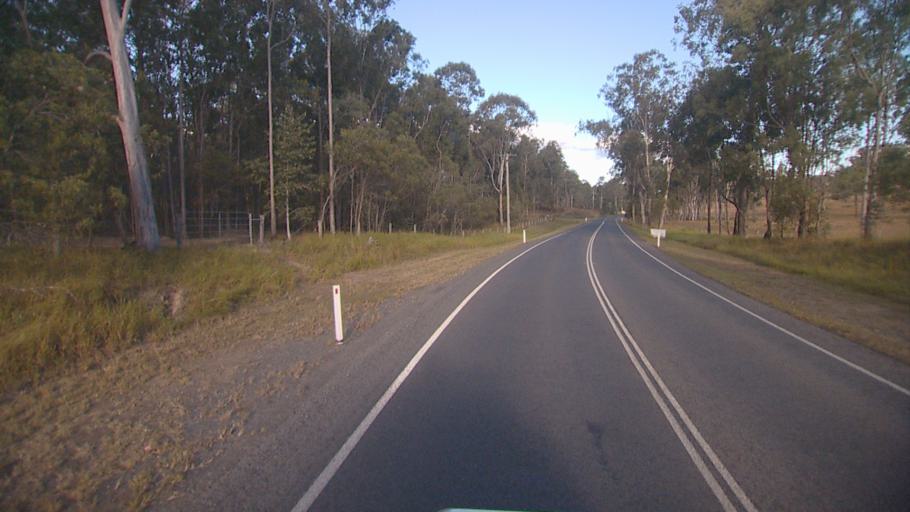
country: AU
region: Queensland
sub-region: Logan
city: Cedar Vale
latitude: -27.8676
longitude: 153.0632
